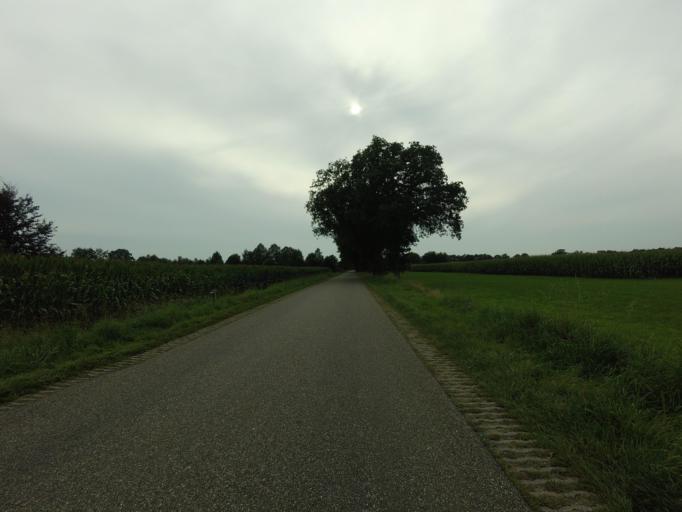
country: NL
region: Gelderland
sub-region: Gemeente Lochem
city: Laren
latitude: 52.2820
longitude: 6.3712
